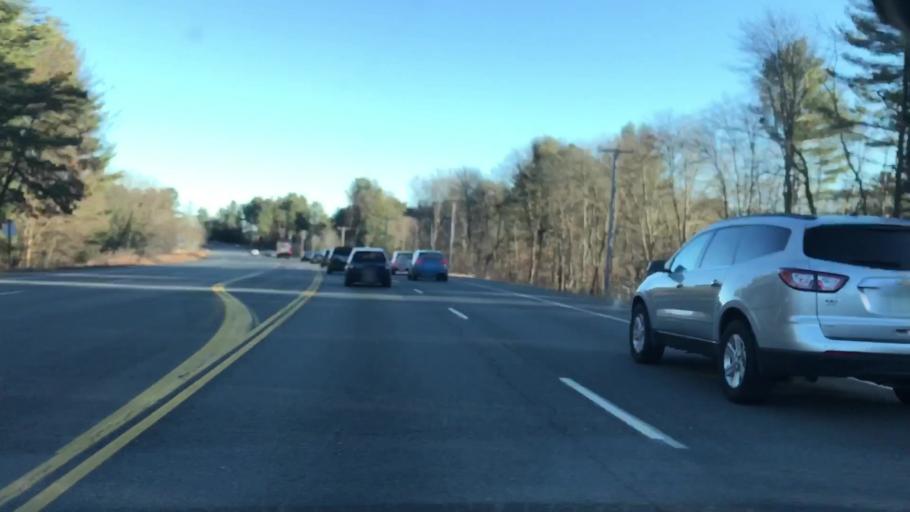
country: US
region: New Hampshire
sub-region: Hillsborough County
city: Hollis
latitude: 42.8041
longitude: -71.5615
